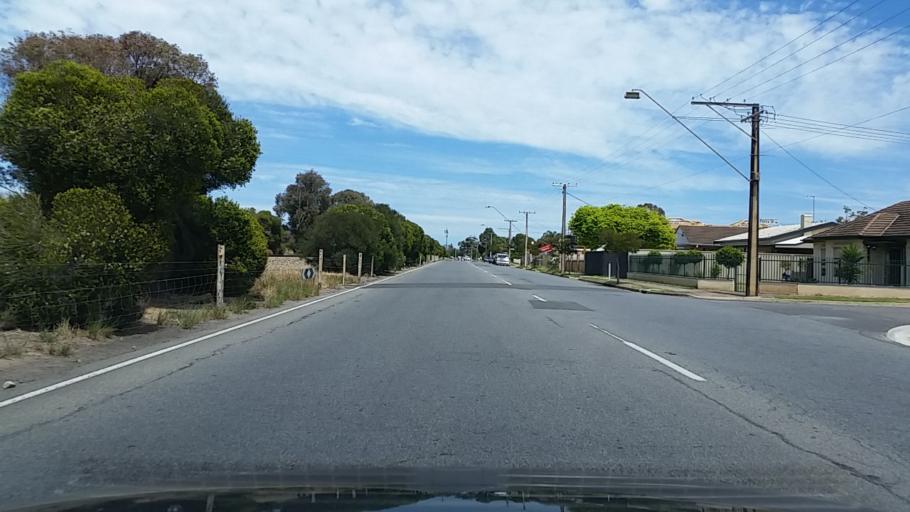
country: AU
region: South Australia
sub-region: Charles Sturt
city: Woodville West
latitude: -34.8863
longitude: 138.5187
